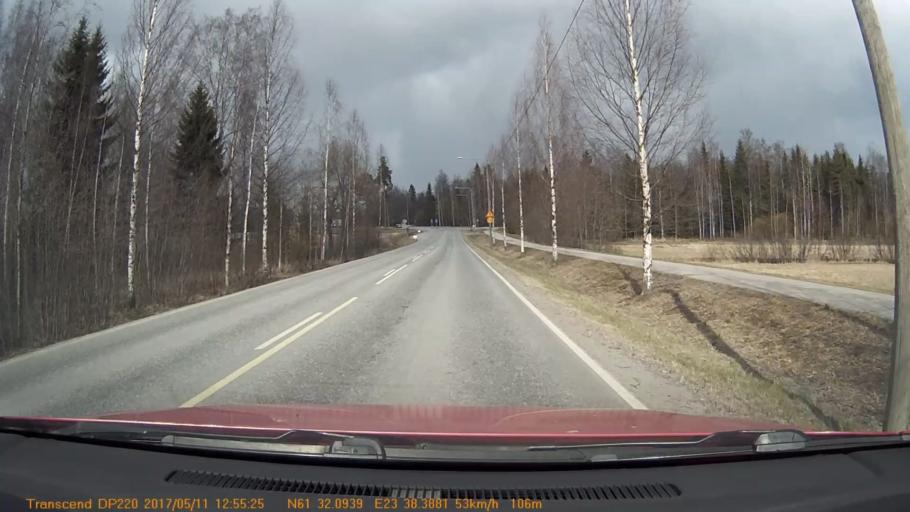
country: FI
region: Pirkanmaa
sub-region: Tampere
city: Yloejaervi
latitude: 61.5349
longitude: 23.6398
